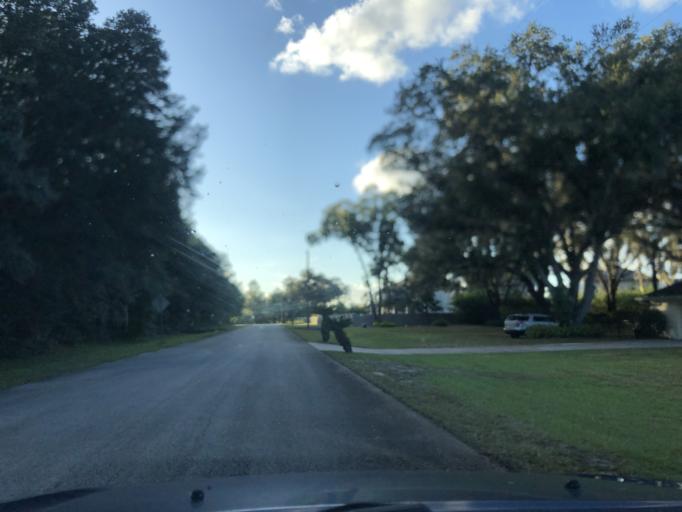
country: US
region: Florida
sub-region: Seminole County
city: Goldenrod
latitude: 28.6150
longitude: -81.2557
